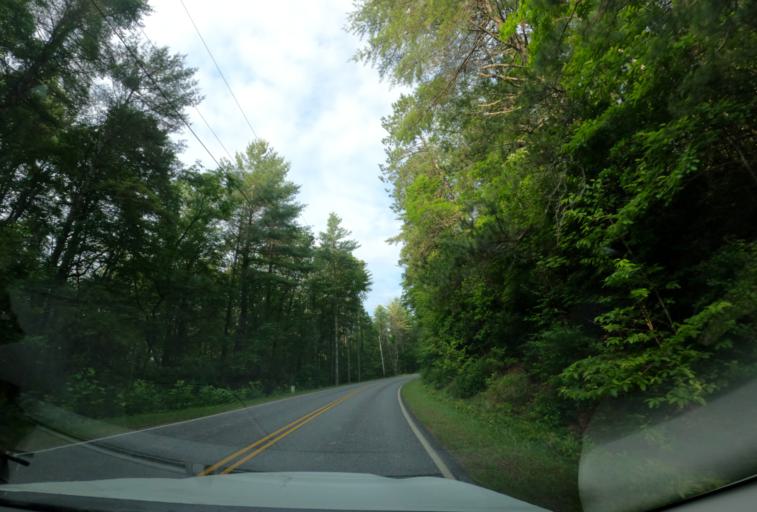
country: US
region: North Carolina
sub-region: Transylvania County
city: Brevard
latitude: 35.1994
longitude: -82.8582
